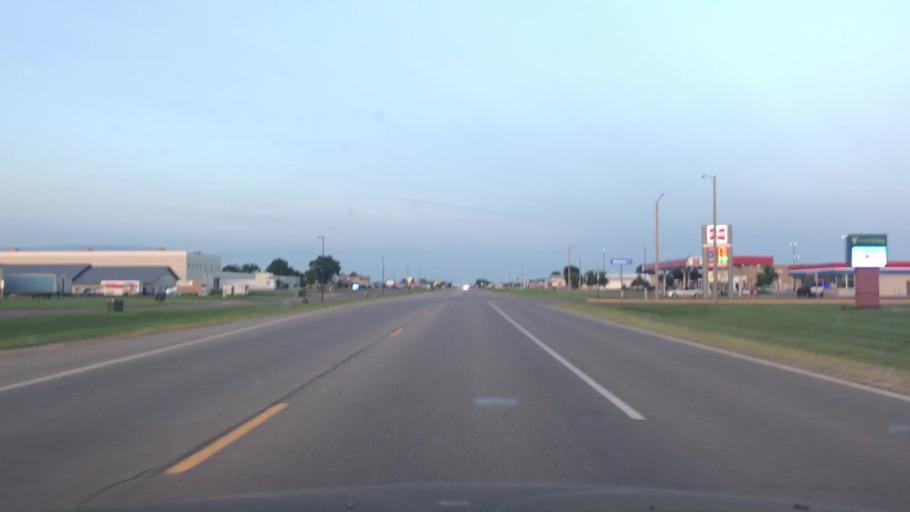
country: US
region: Minnesota
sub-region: Redwood County
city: Redwood Falls
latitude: 44.5414
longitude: -95.0914
